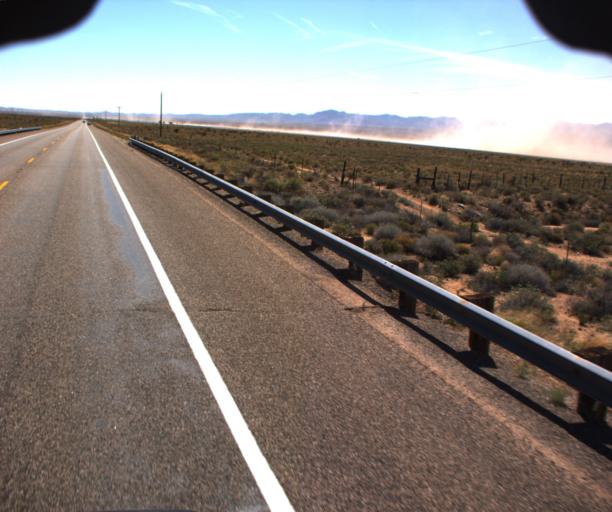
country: US
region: Arizona
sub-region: Mohave County
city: New Kingman-Butler
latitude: 35.3678
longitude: -113.8666
